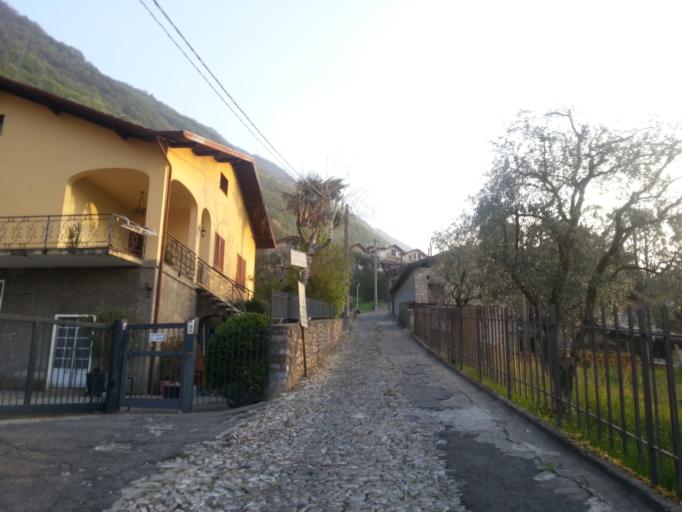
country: IT
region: Lombardy
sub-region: Provincia di Como
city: Lenno
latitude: 45.9757
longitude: 9.1860
